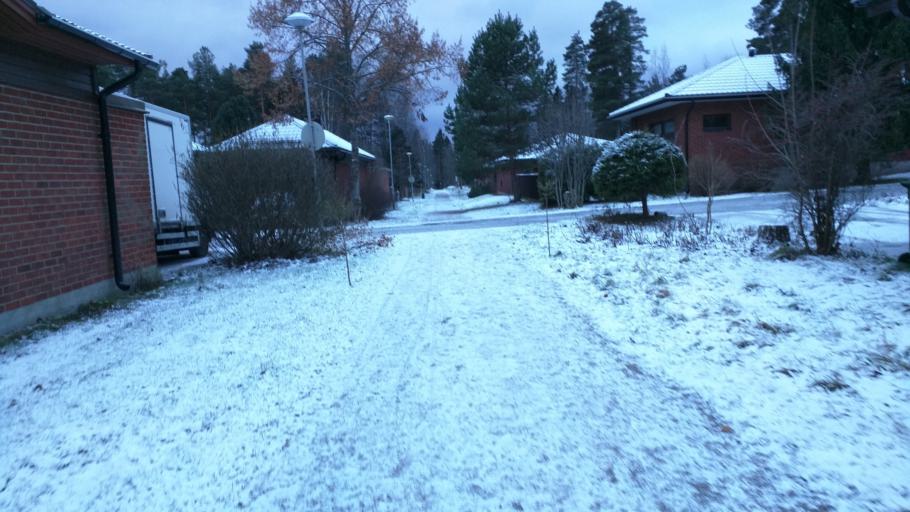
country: FI
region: Uusimaa
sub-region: Helsinki
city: Kilo
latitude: 60.2447
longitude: 24.7664
